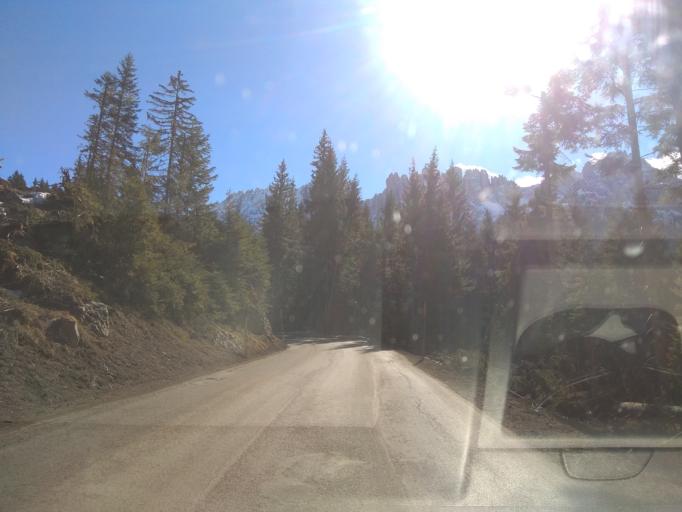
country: IT
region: Trentino-Alto Adige
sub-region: Bolzano
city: Nova Levante
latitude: 46.4122
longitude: 11.5656
